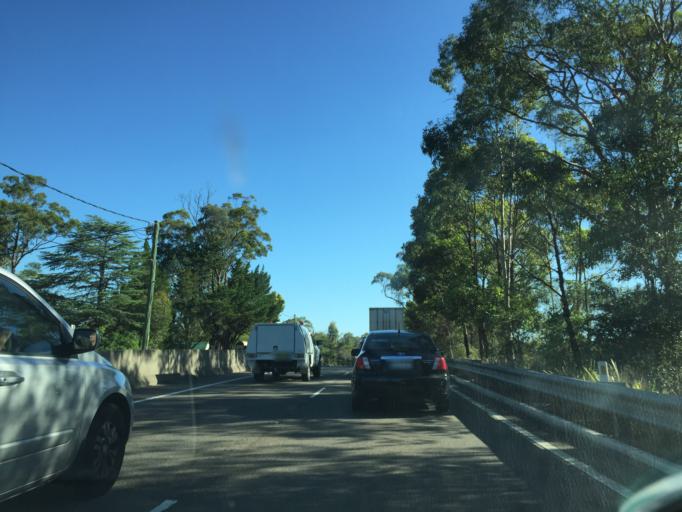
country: AU
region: New South Wales
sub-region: Blue Mountains Municipality
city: Blaxland
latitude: -33.7160
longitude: 150.5937
